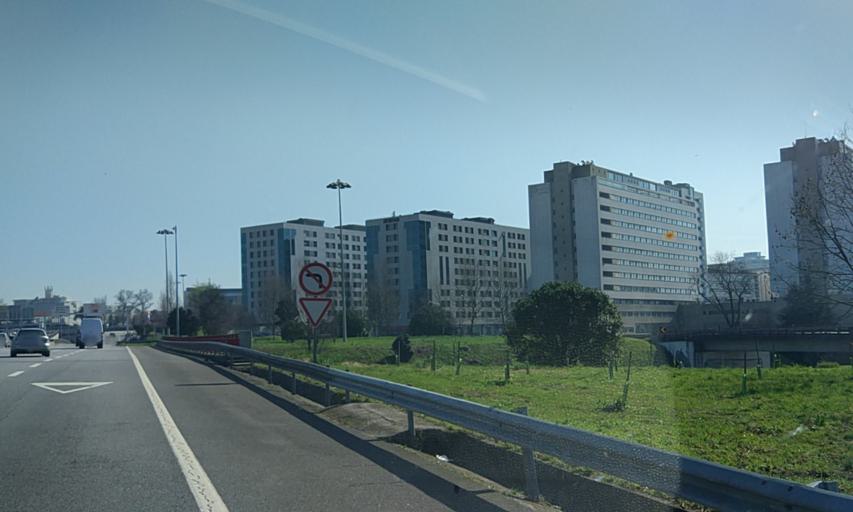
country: PT
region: Porto
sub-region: Matosinhos
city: Senhora da Hora
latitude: 41.1671
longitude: -8.6383
